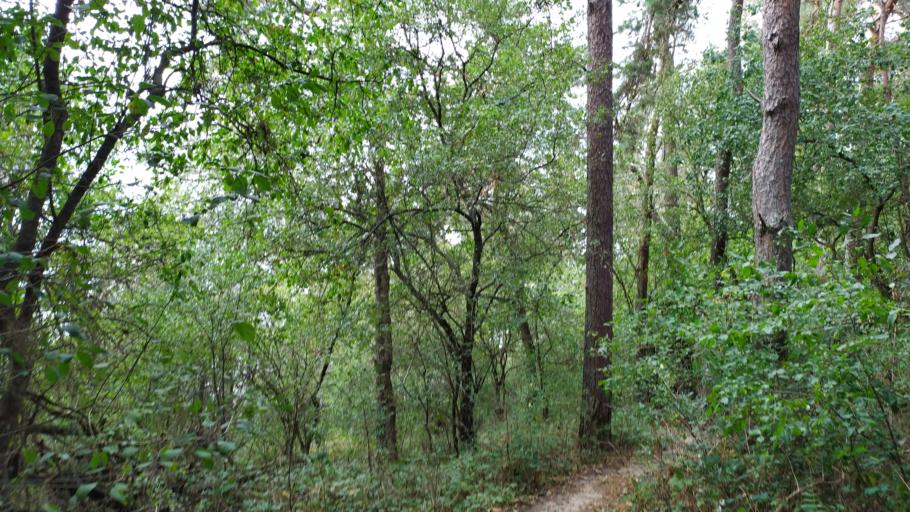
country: DE
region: Mecklenburg-Vorpommern
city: Lassan
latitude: 54.0067
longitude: 13.8540
